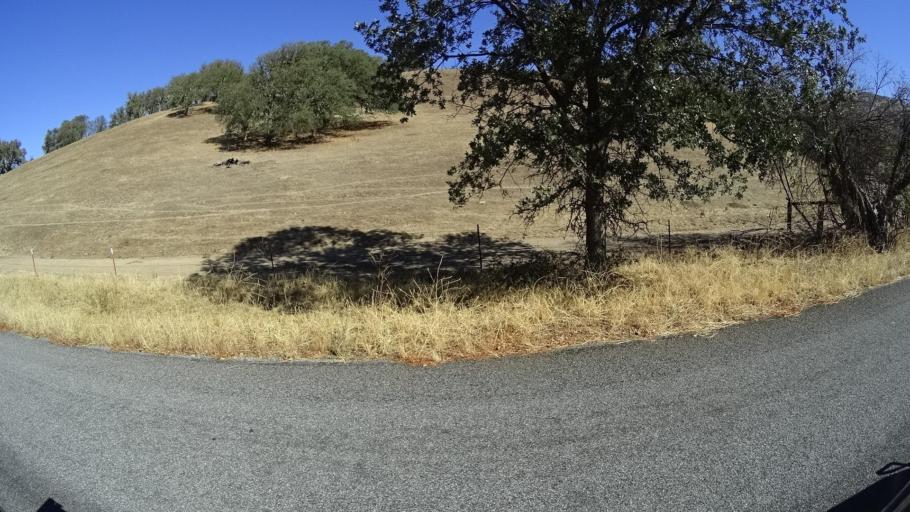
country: US
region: California
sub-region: Monterey County
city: Gonzales
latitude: 36.3941
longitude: -121.5701
